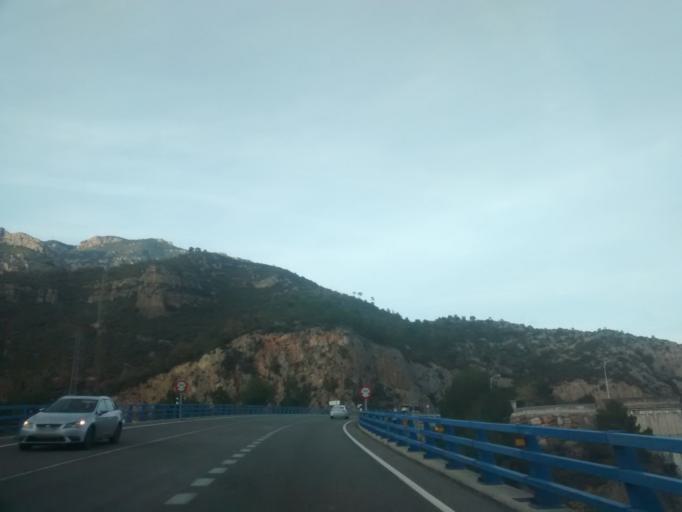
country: ES
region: Catalonia
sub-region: Provincia de Lleida
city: Oliana
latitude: 42.0919
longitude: 1.2921
